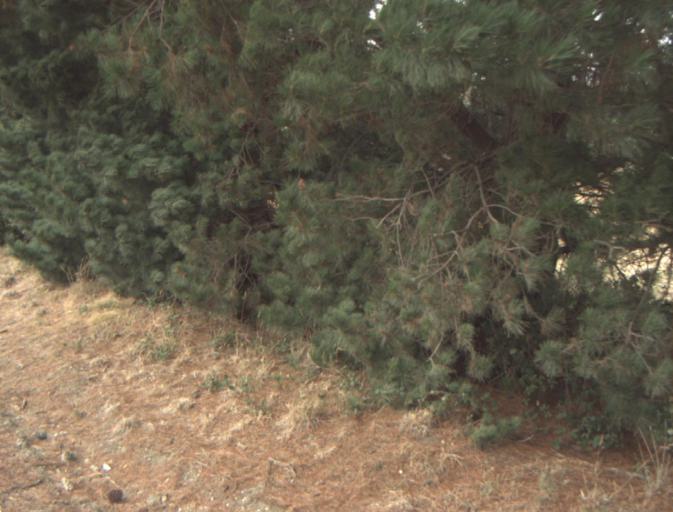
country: AU
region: Tasmania
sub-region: Launceston
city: Mayfield
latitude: -41.1713
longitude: 147.2128
